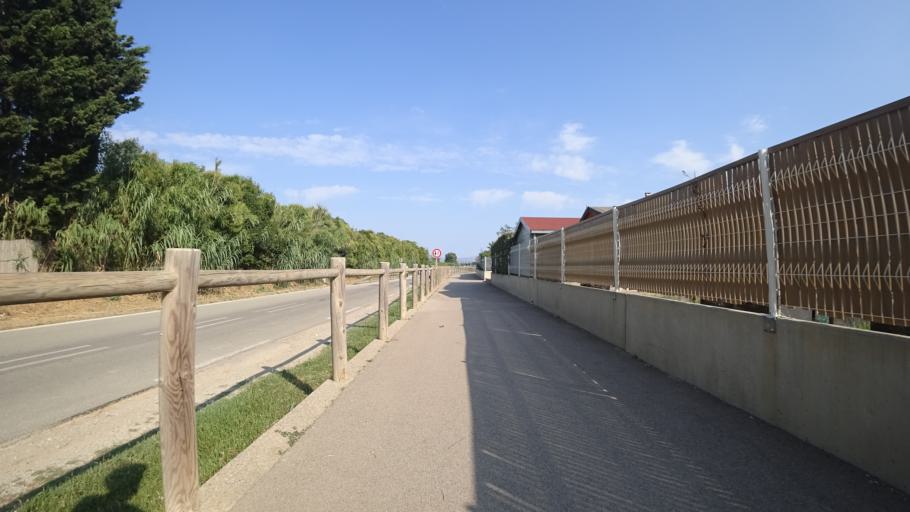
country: FR
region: Languedoc-Roussillon
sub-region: Departement des Pyrenees-Orientales
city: Saint-Laurent-de-la-Salanque
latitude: 42.7674
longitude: 2.9808
